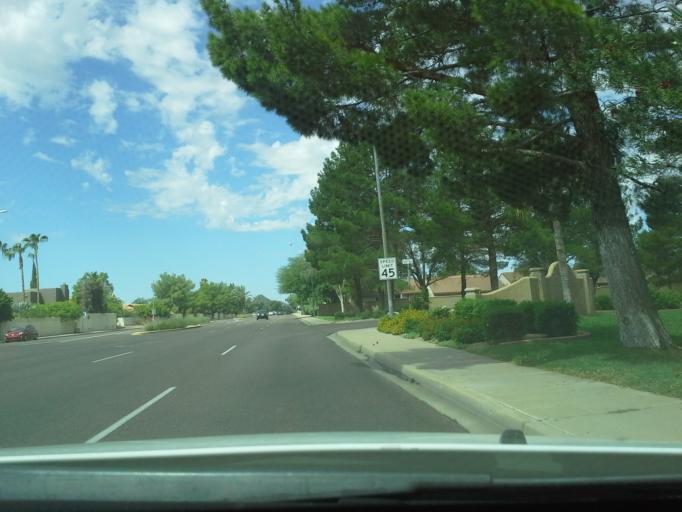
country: US
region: Arizona
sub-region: Maricopa County
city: Paradise Valley
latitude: 33.6262
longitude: -111.9712
